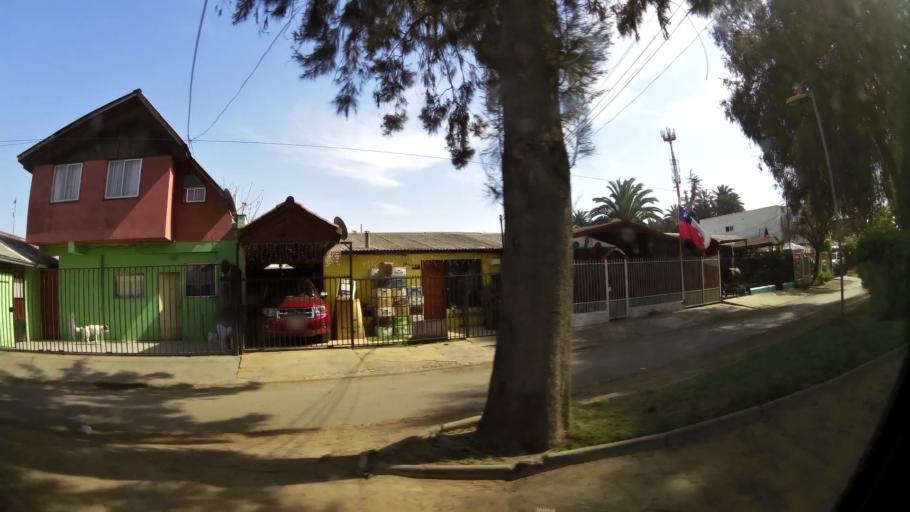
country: CL
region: Santiago Metropolitan
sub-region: Provincia de Santiago
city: Lo Prado
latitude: -33.4796
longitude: -70.7417
